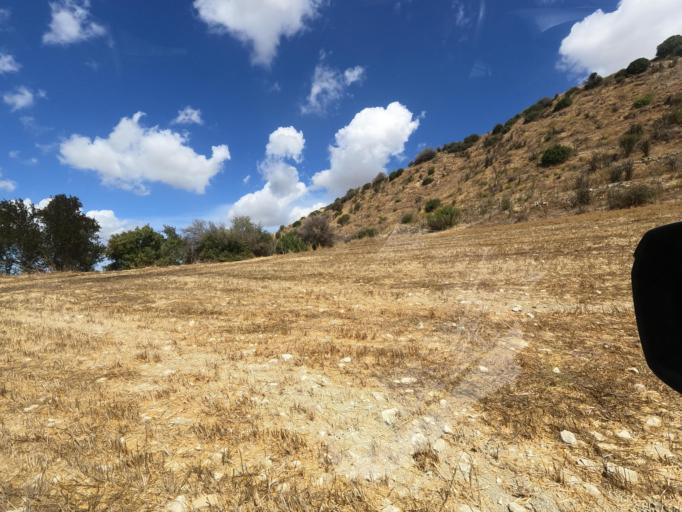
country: CY
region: Pafos
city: Mesogi
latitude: 34.8305
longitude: 32.5468
